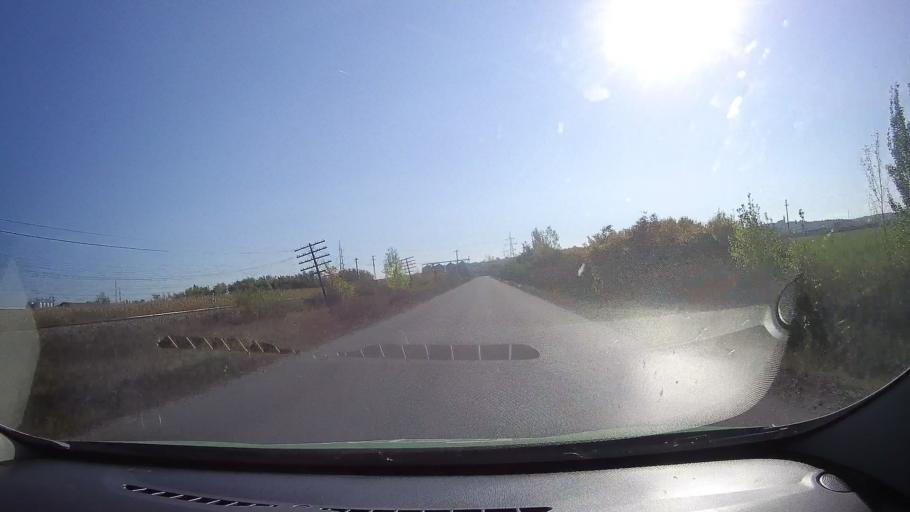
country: RO
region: Satu Mare
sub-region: Oras Tasnad
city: Tasnad
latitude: 47.4940
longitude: 22.5680
